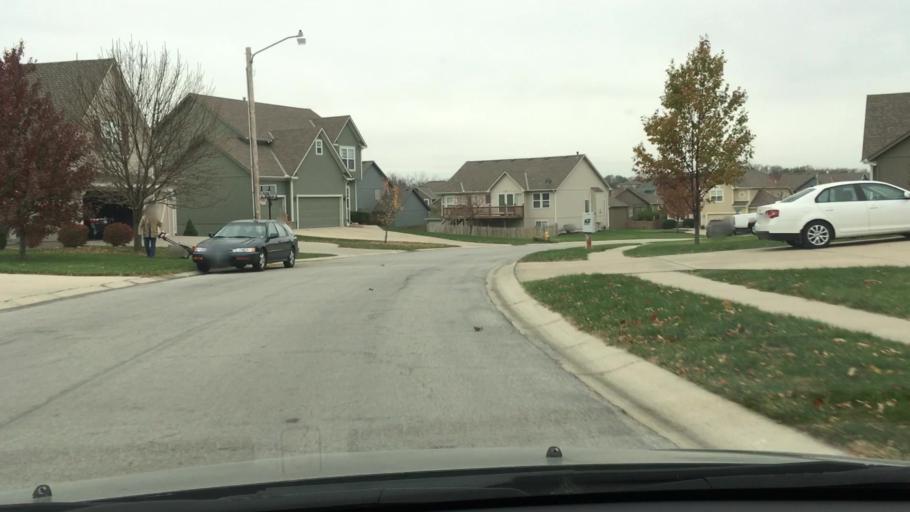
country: US
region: Missouri
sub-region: Jackson County
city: Lees Summit
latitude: 38.8771
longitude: -94.4269
